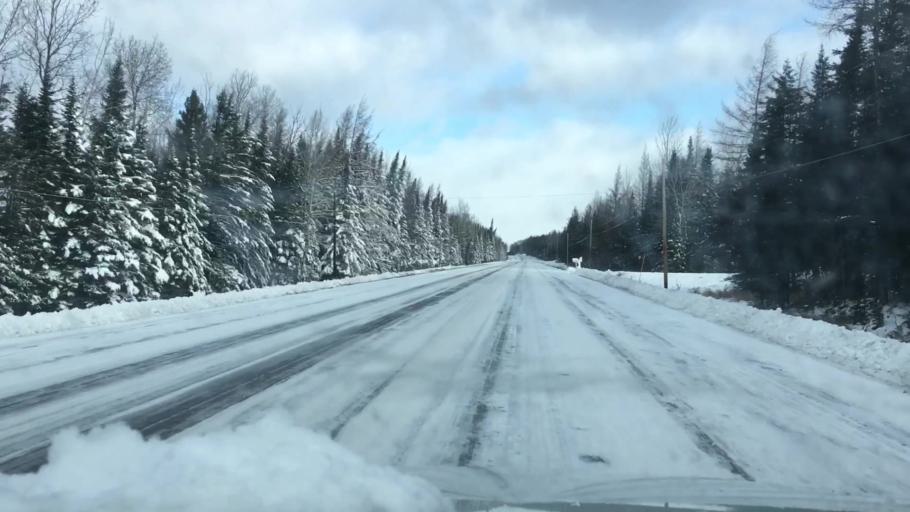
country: US
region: Maine
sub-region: Aroostook County
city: Van Buren
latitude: 47.0275
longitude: -68.0099
